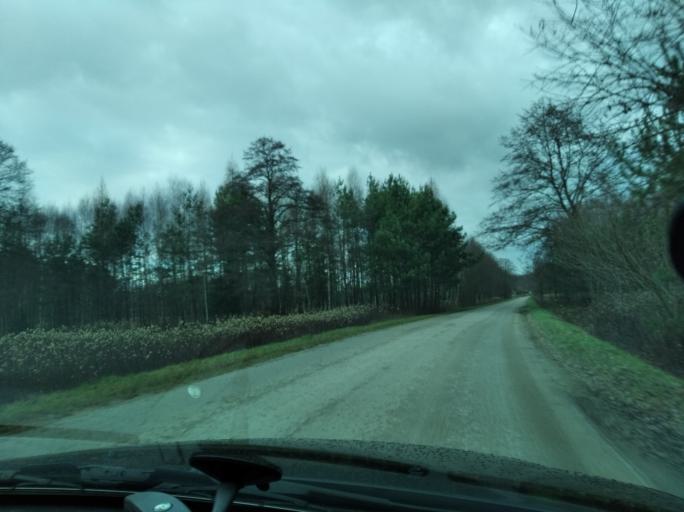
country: PL
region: Subcarpathian Voivodeship
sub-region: Powiat lancucki
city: Zolynia
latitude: 50.1409
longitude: 22.2798
